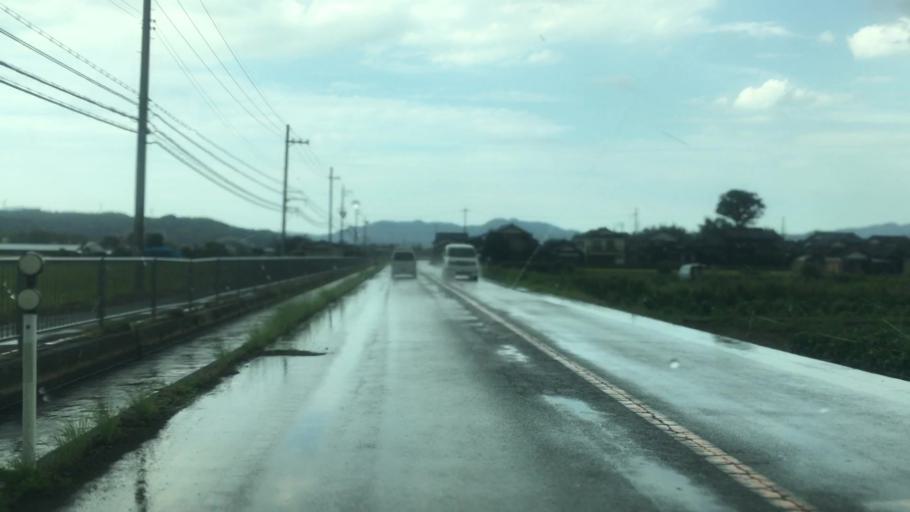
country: JP
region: Hyogo
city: Toyooka
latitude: 35.4951
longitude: 134.8161
